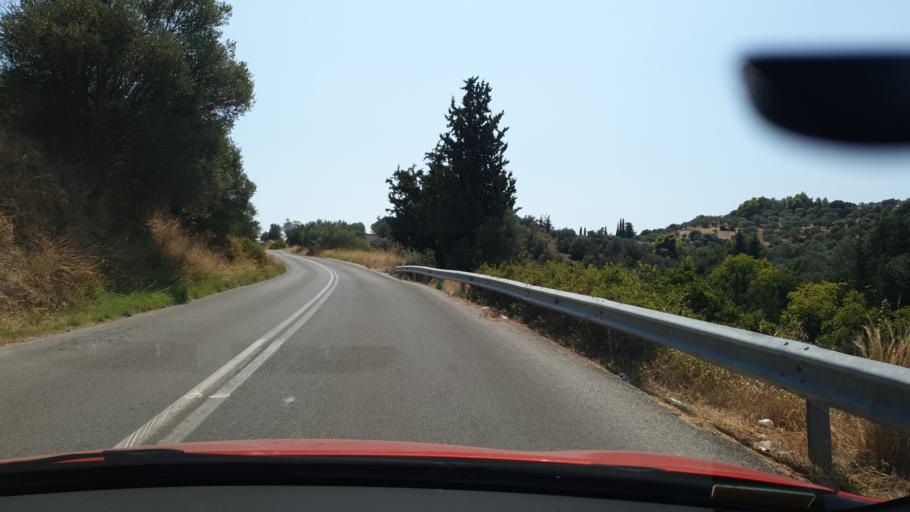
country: GR
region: Central Greece
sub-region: Nomos Evvoias
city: Oxilithos
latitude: 38.5248
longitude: 24.0922
